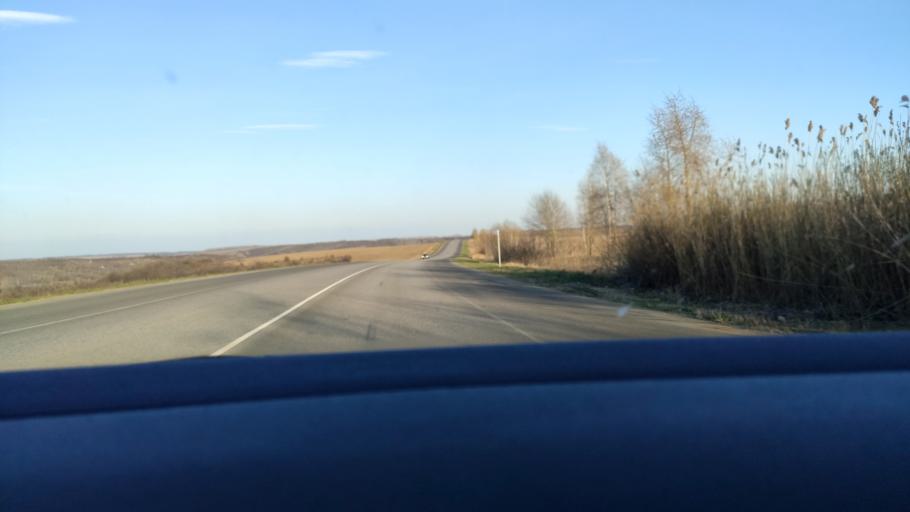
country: RU
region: Voronezj
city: Kolodeznyy
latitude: 51.3393
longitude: 39.0736
